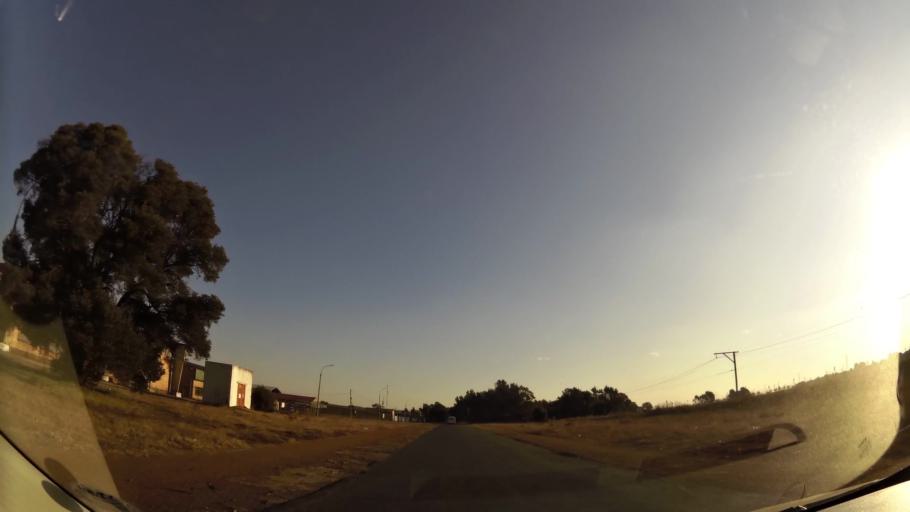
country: ZA
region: Gauteng
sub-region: West Rand District Municipality
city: Randfontein
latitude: -26.1932
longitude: 27.6836
